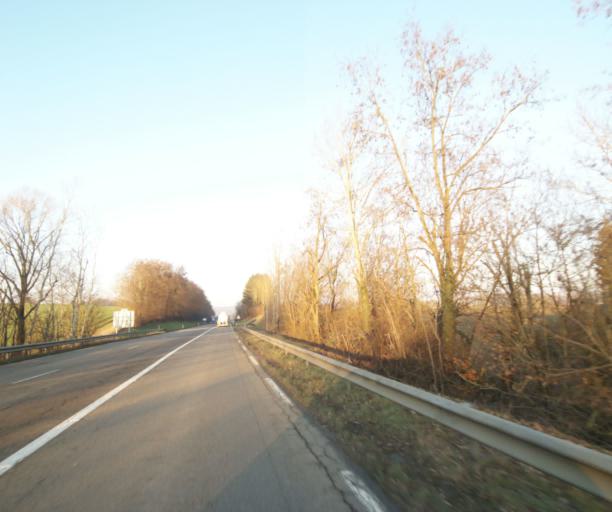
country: FR
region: Champagne-Ardenne
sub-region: Departement de la Haute-Marne
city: Bienville
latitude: 48.5865
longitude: 5.0289
